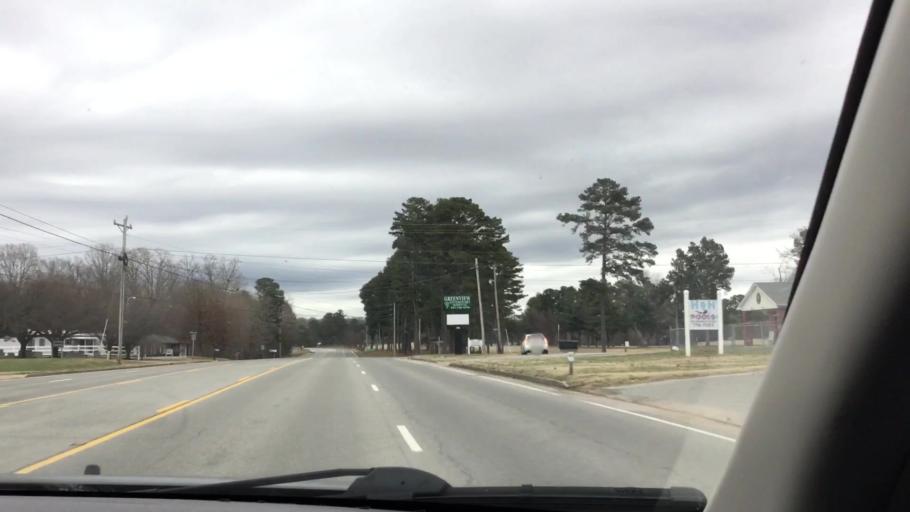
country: US
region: Tennessee
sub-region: Lewis County
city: Hohenwald
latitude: 35.5644
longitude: -87.5088
